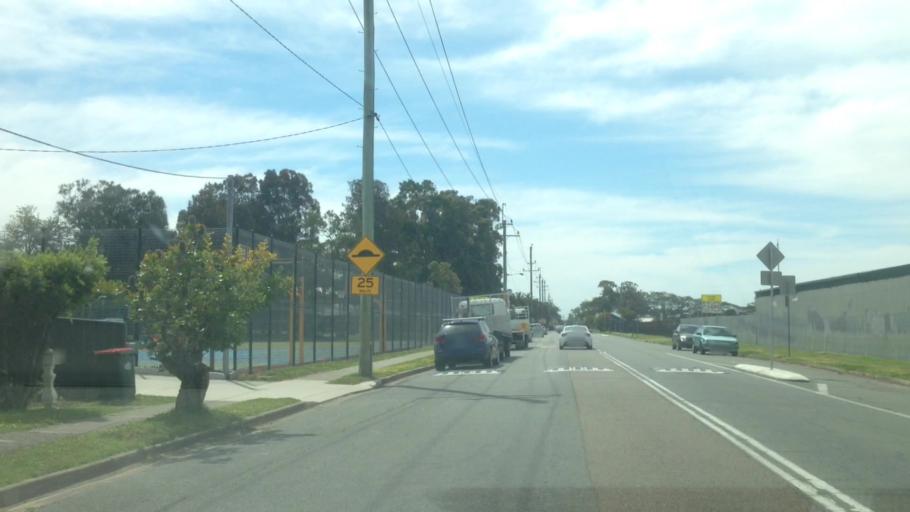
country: AU
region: New South Wales
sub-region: Newcastle
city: Broadmeadow
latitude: -32.9311
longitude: 151.7360
